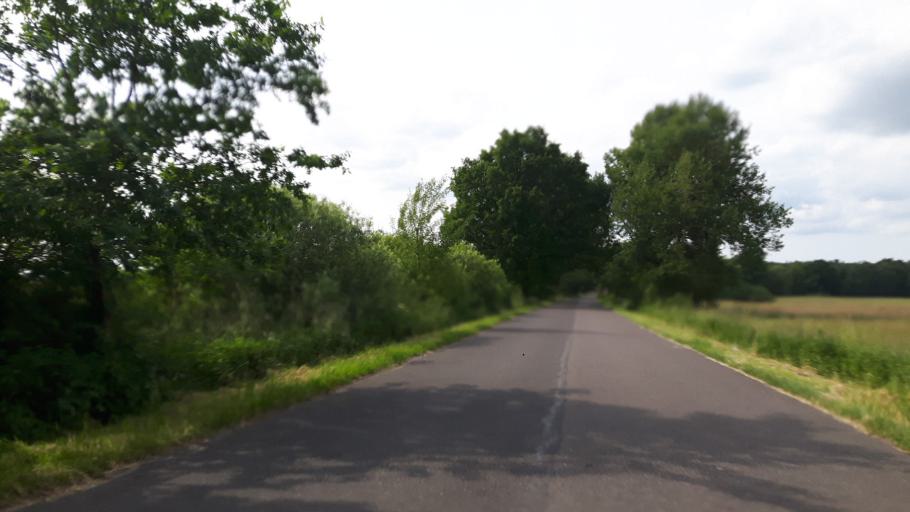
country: PL
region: West Pomeranian Voivodeship
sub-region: Powiat goleniowski
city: Nowogard
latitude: 53.7721
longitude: 15.1236
